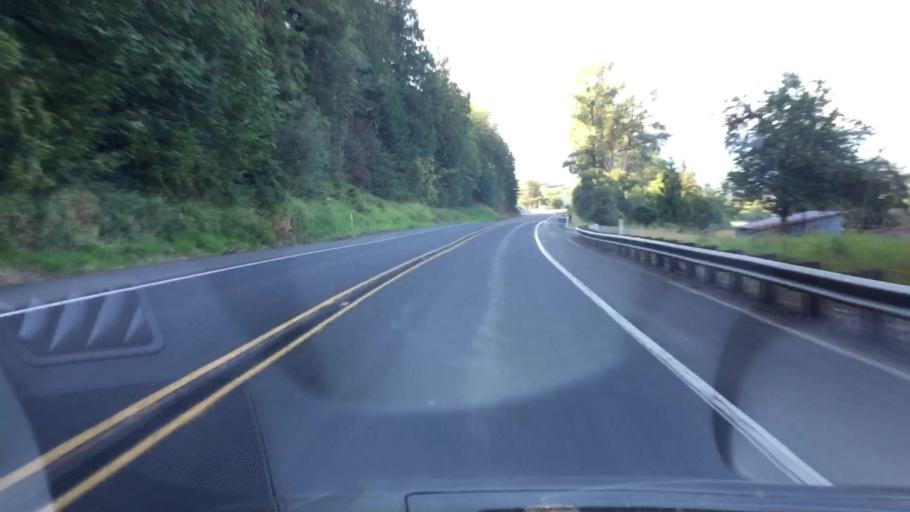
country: US
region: Washington
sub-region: Lewis County
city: Morton
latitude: 46.5284
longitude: -122.2372
